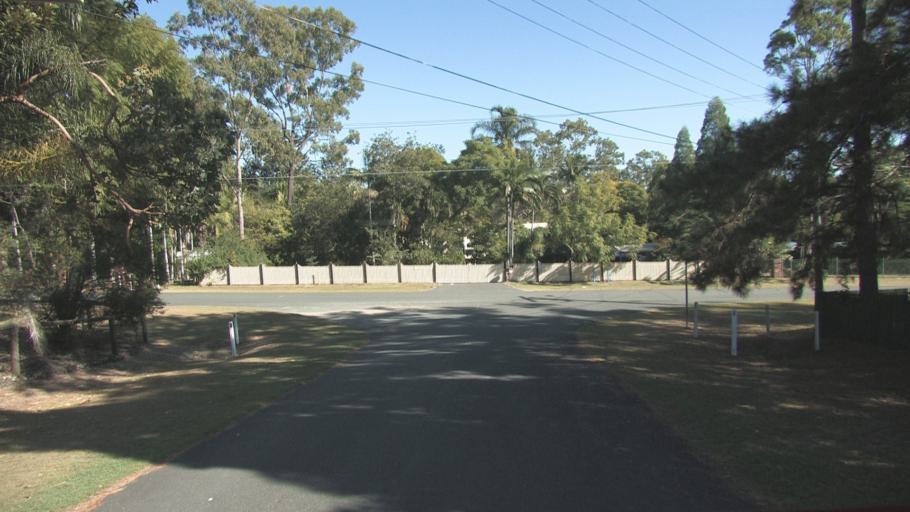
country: AU
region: Queensland
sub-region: Brisbane
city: Forest Lake
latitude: -27.6647
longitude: 153.0114
